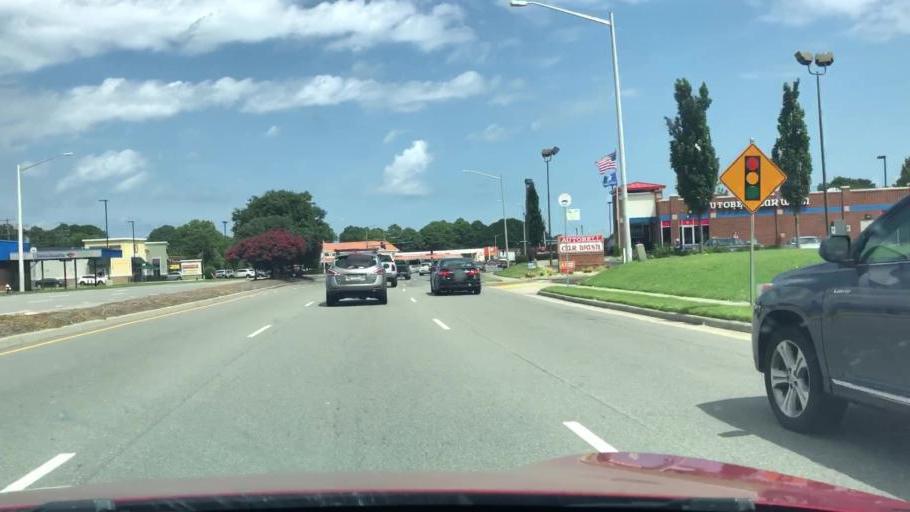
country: US
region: Virginia
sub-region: City of Chesapeake
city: Chesapeake
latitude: 36.8735
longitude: -76.1343
